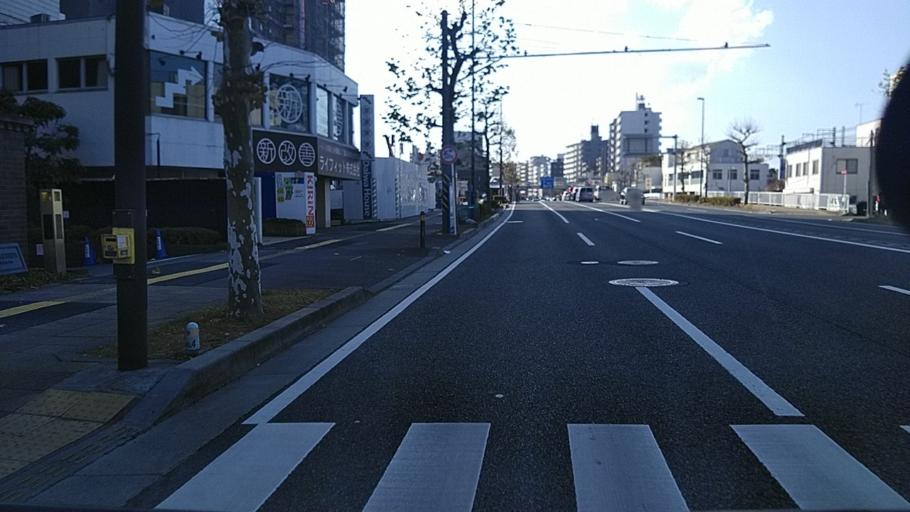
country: JP
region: Kanagawa
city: Yokohama
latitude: 35.4851
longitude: 139.6509
